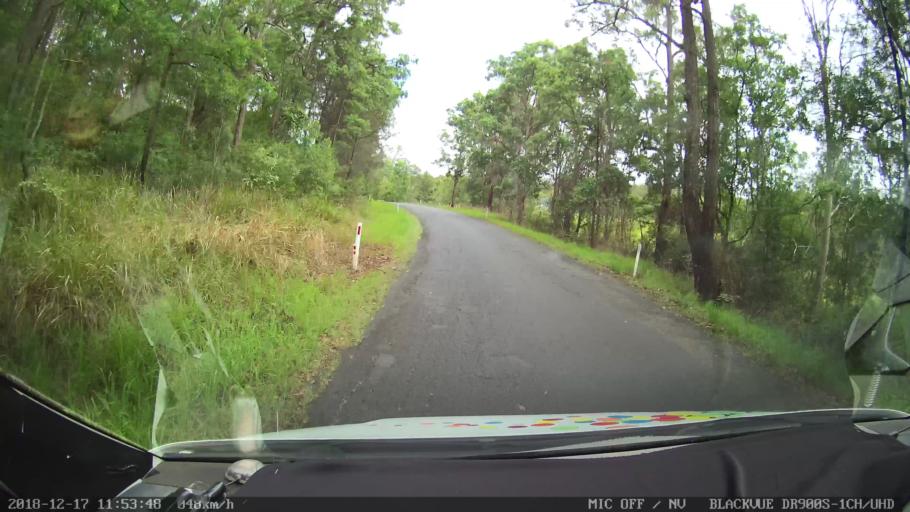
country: AU
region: New South Wales
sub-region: Kyogle
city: Kyogle
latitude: -28.5718
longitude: 152.5857
